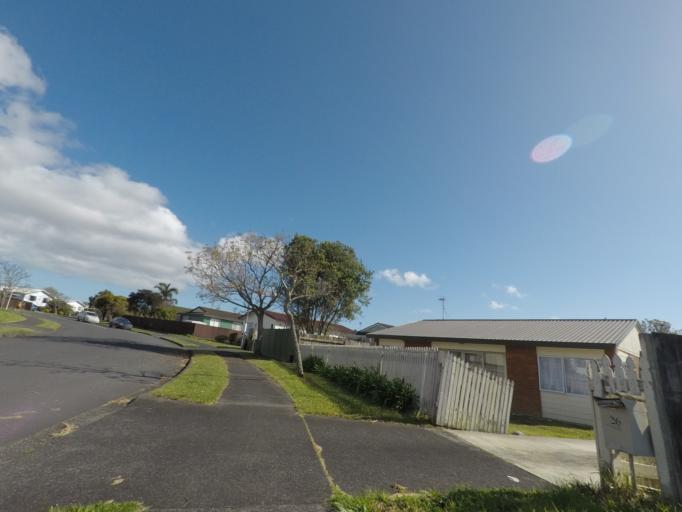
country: NZ
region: Auckland
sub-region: Auckland
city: Rosebank
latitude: -36.8604
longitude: 174.6020
